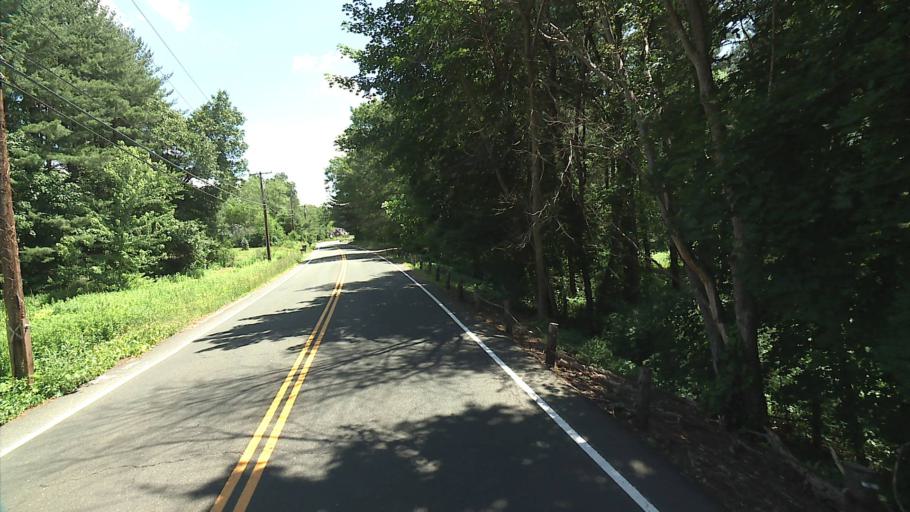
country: US
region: Connecticut
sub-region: Tolland County
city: Somers
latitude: 41.9929
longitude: -72.4856
